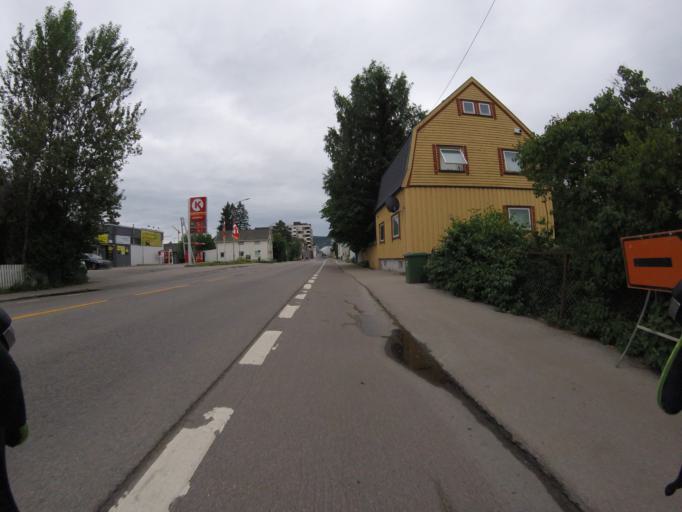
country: NO
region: Akershus
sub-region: Skedsmo
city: Lillestrom
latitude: 59.9617
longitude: 11.0503
